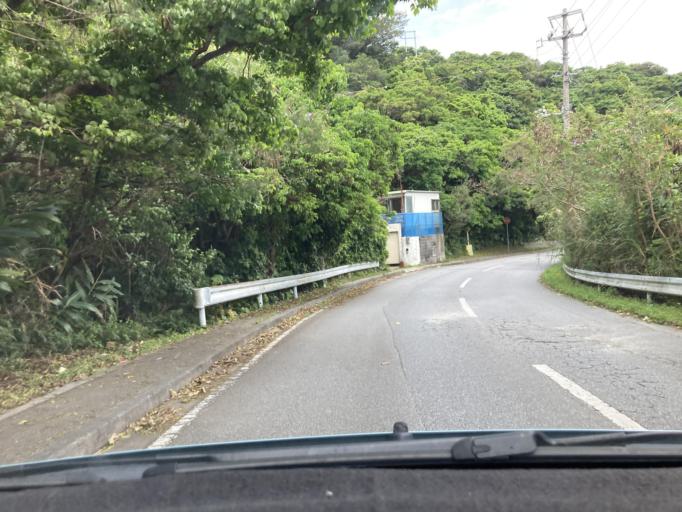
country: JP
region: Okinawa
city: Ginowan
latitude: 26.2304
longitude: 127.7473
